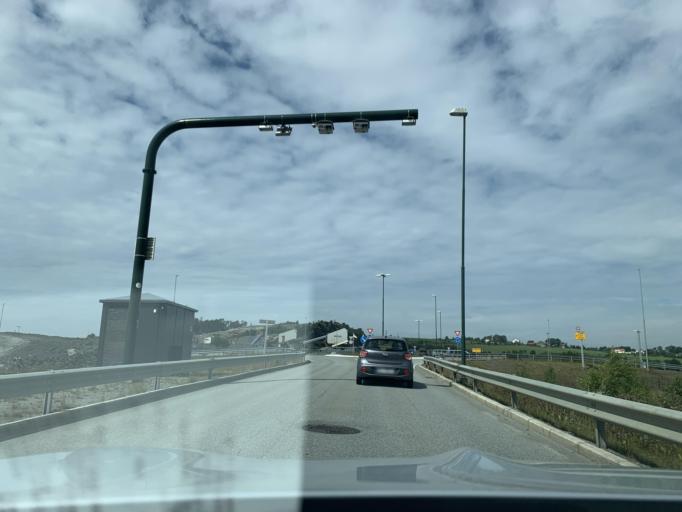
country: NO
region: Rogaland
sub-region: Sola
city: Sola
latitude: 58.8957
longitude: 5.6775
